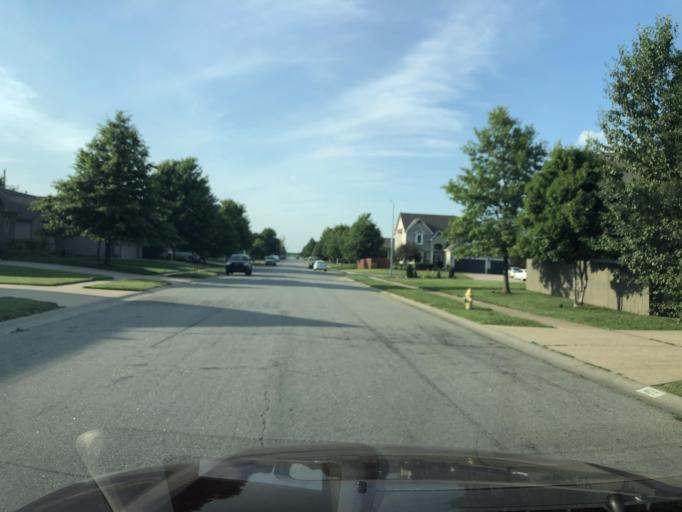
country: US
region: Kansas
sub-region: Johnson County
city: Gardner
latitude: 38.8201
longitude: -94.9362
